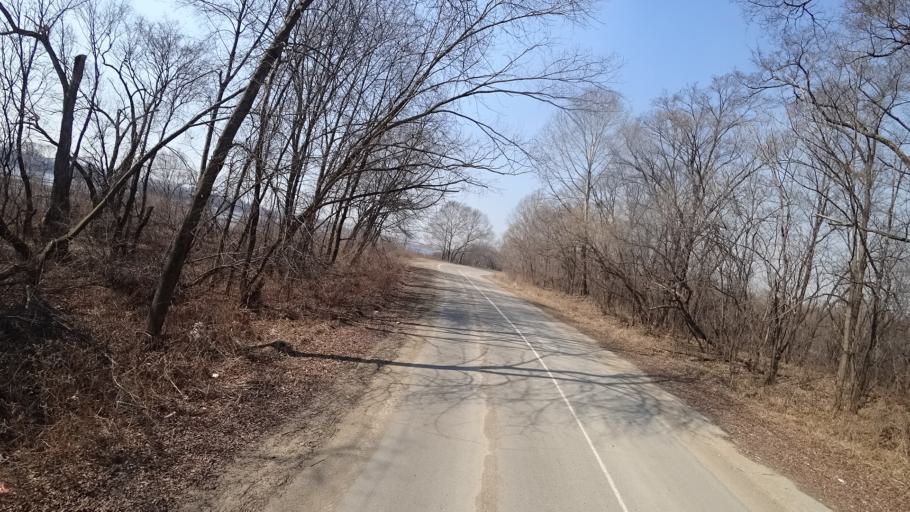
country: RU
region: Amur
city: Novobureyskiy
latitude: 49.7902
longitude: 129.9065
